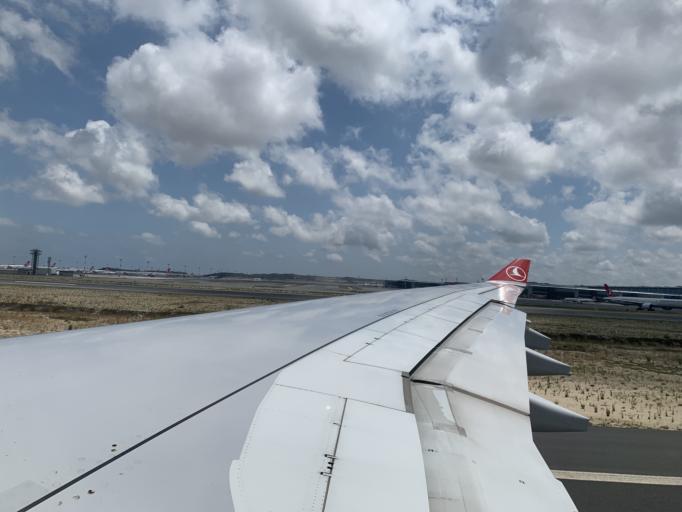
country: TR
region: Istanbul
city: Durusu
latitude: 41.2691
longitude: 28.7255
